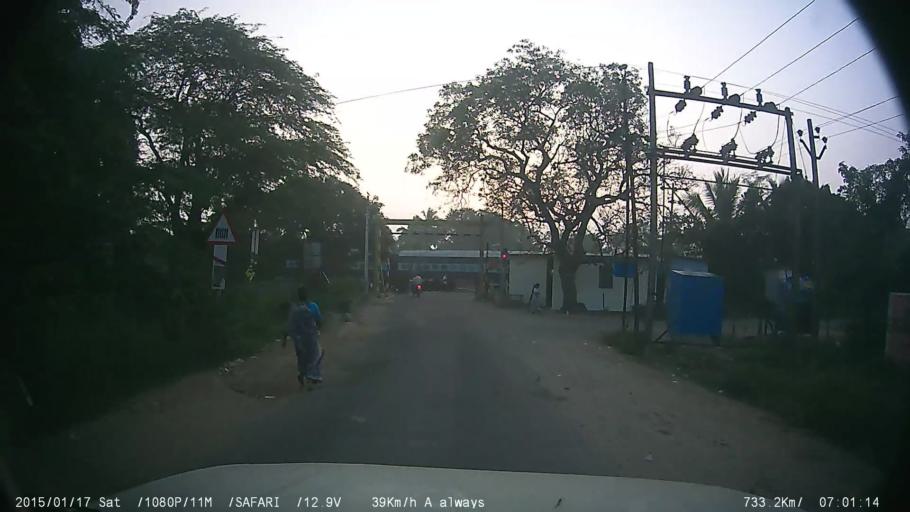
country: IN
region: Tamil Nadu
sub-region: Kancheepuram
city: Singapperumalkovil
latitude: 12.7953
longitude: 80.0180
